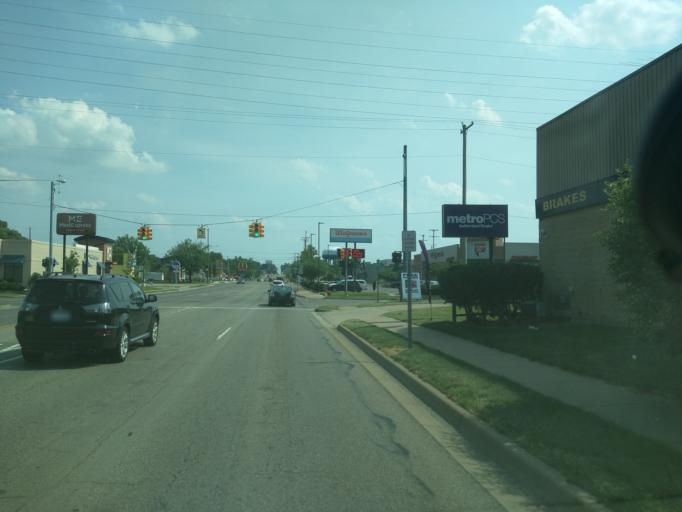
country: US
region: Michigan
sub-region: Jackson County
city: Jackson
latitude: 42.2656
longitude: -84.4234
